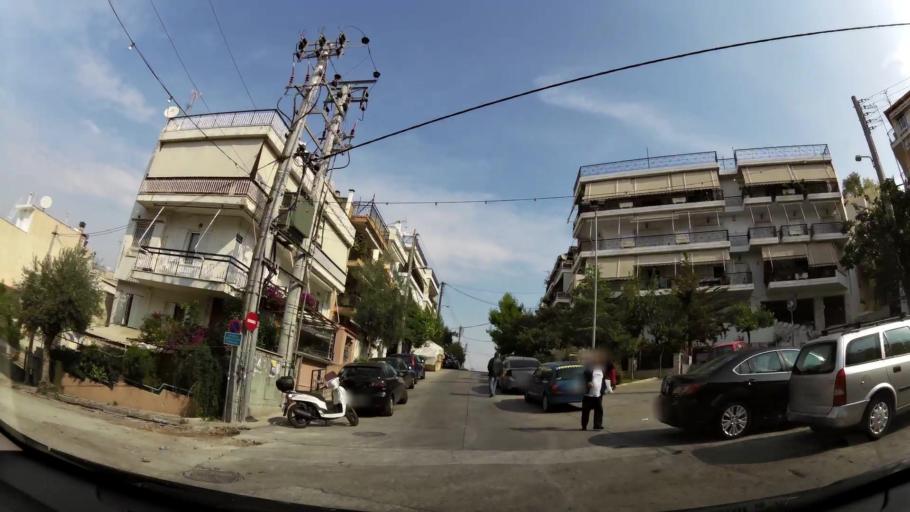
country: GR
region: Attica
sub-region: Nomarchia Athinas
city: Galatsi
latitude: 38.0082
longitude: 23.7538
